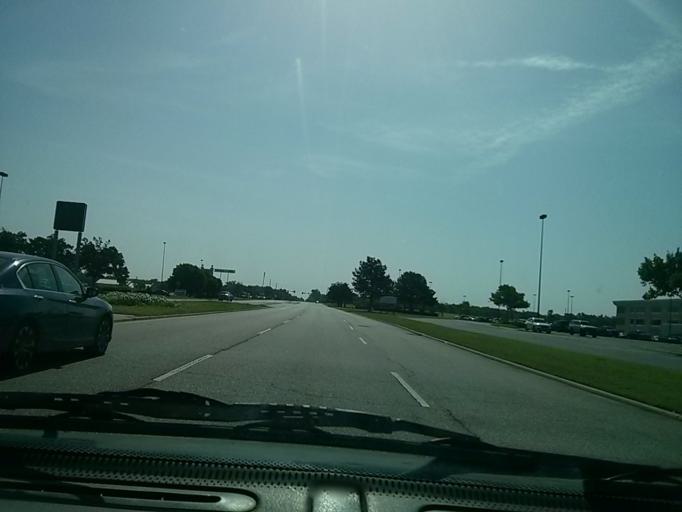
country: US
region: Oklahoma
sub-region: Tulsa County
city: Broken Arrow
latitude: 36.1334
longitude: -95.8201
